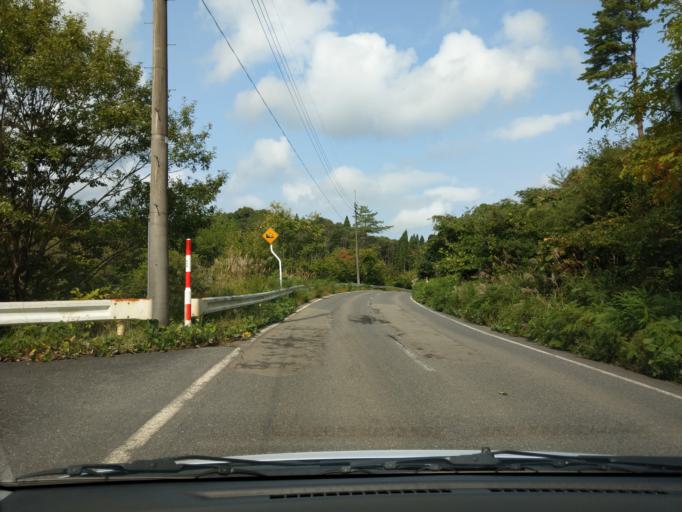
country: JP
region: Akita
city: Omagari
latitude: 39.4618
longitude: 140.3173
